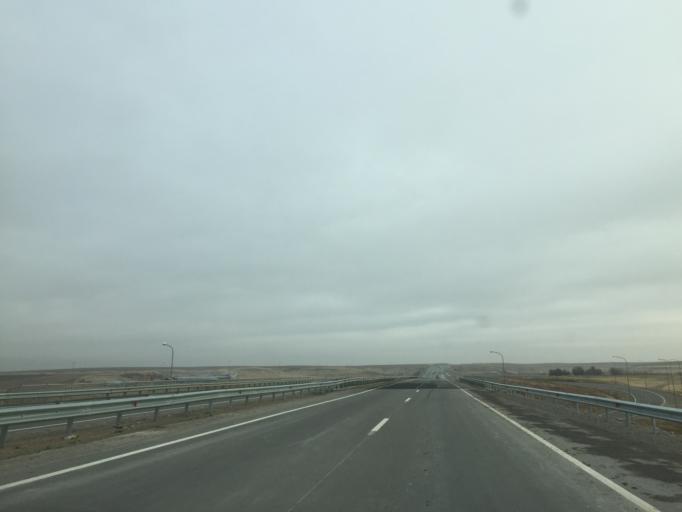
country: KZ
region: Ongtustik Qazaqstan
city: Aksu
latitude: 42.4369
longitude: 69.7199
